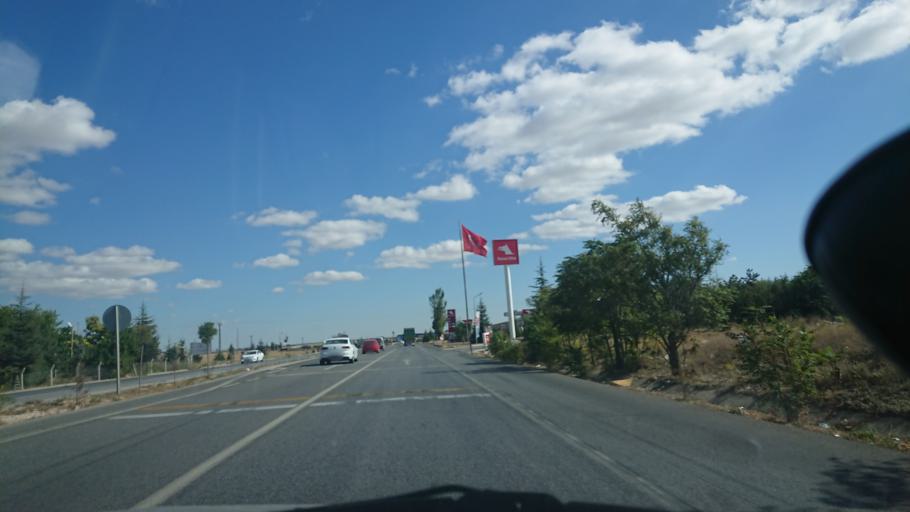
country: TR
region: Eskisehir
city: Mahmudiye
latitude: 39.5857
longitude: 30.8997
